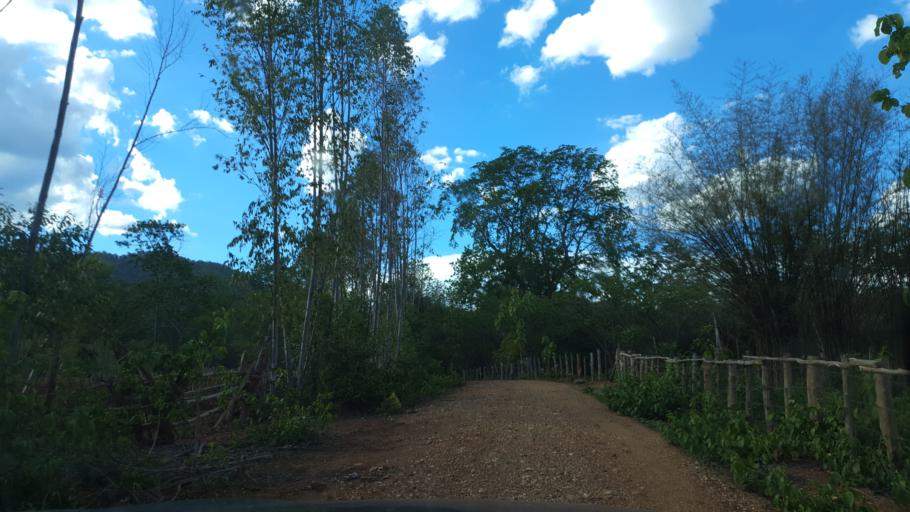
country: TH
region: Lampang
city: Sop Prap
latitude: 17.8485
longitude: 99.2848
